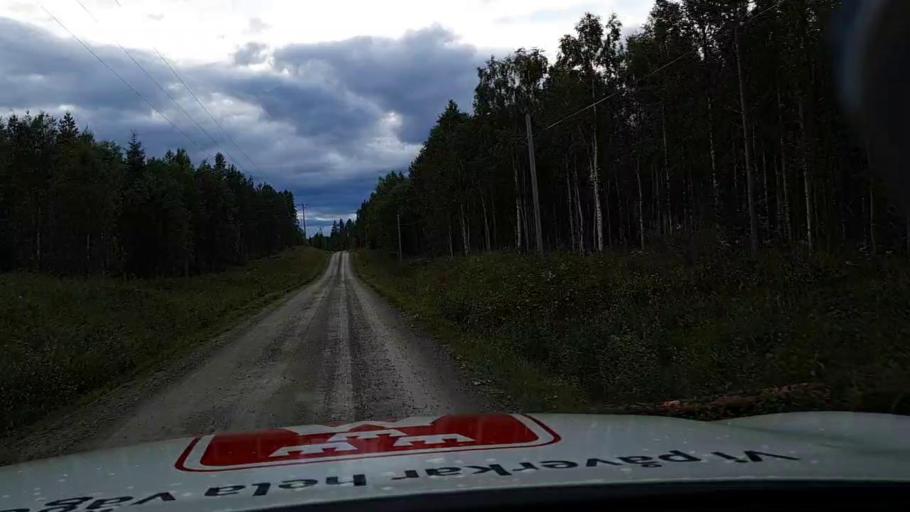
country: SE
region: Jaemtland
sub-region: Bergs Kommun
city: Hoverberg
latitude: 62.8916
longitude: 14.5615
